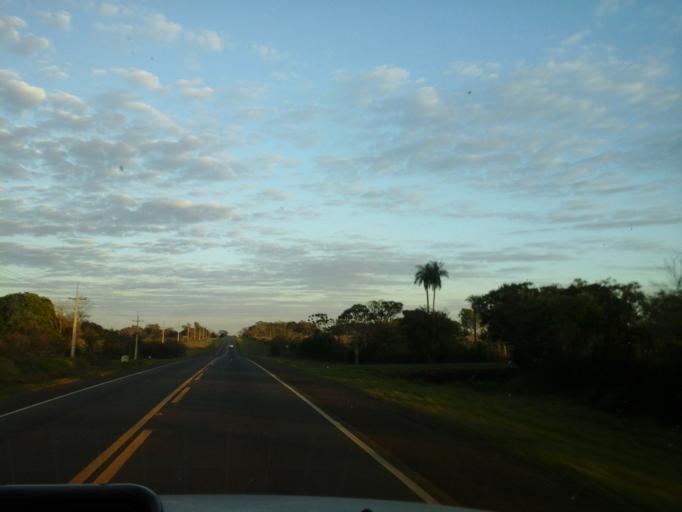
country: PY
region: Misiones
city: San Patricio
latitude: -27.0301
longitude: -56.6902
